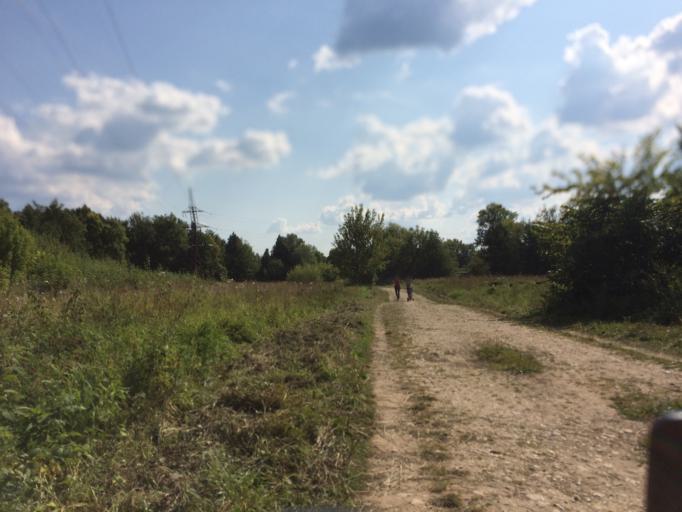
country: RU
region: Mariy-El
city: Yoshkar-Ola
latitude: 56.6147
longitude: 47.9315
